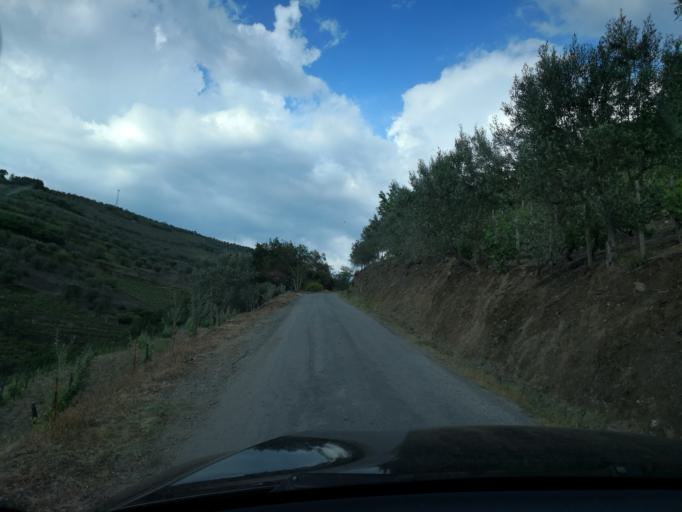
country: PT
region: Vila Real
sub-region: Vila Real
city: Vila Real
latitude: 41.2190
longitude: -7.7111
